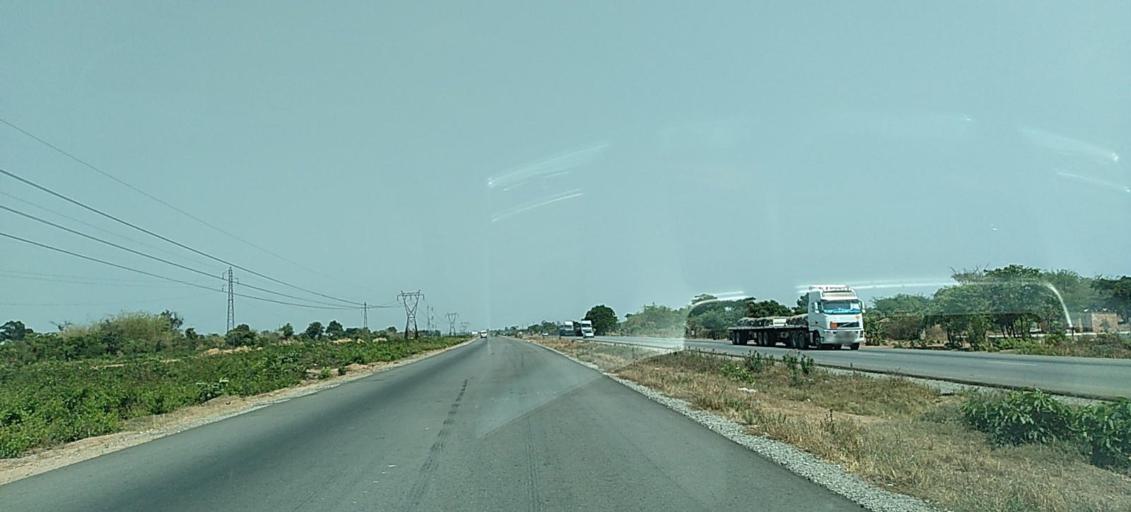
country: ZM
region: Copperbelt
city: Chambishi
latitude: -12.6047
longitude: 27.9710
